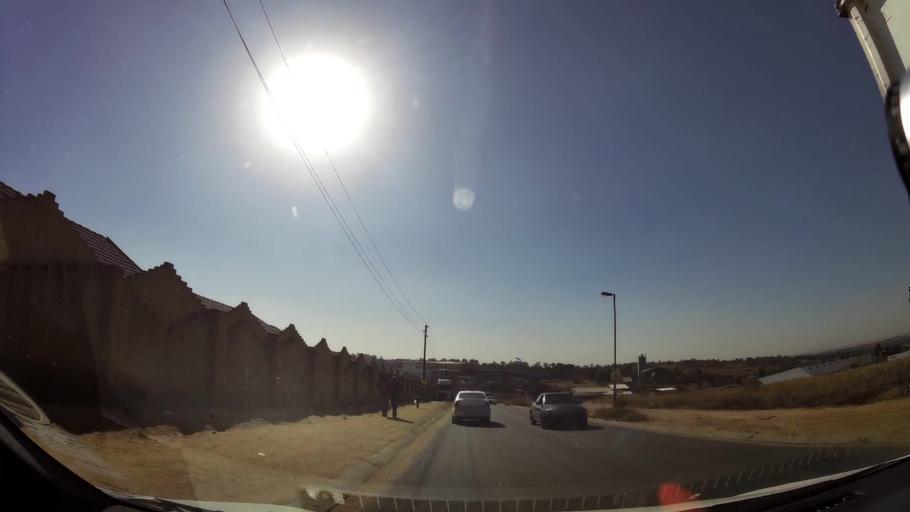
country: ZA
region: Gauteng
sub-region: City of Johannesburg Metropolitan Municipality
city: Diepsloot
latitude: -26.0120
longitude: 27.9434
